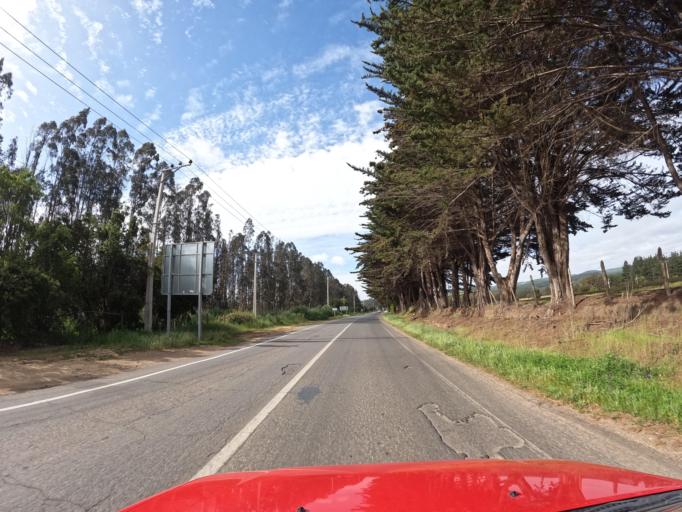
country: CL
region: O'Higgins
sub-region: Provincia de Colchagua
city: Santa Cruz
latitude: -34.3800
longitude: -71.9729
